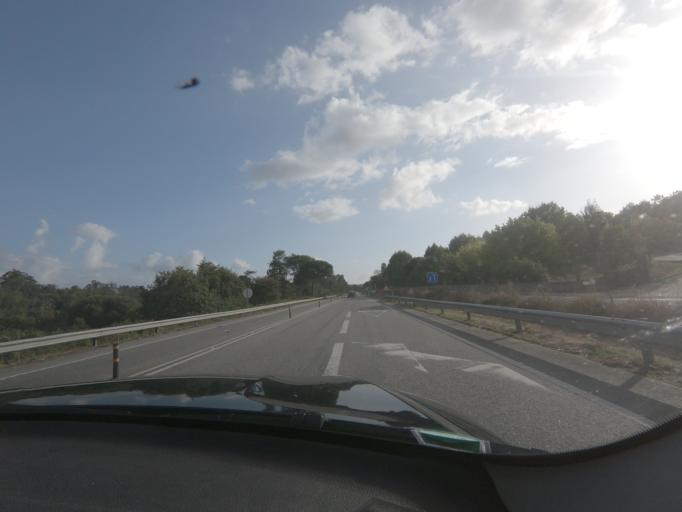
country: PT
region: Viseu
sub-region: Concelho de Tondela
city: Tondela
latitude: 40.5332
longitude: -8.0629
